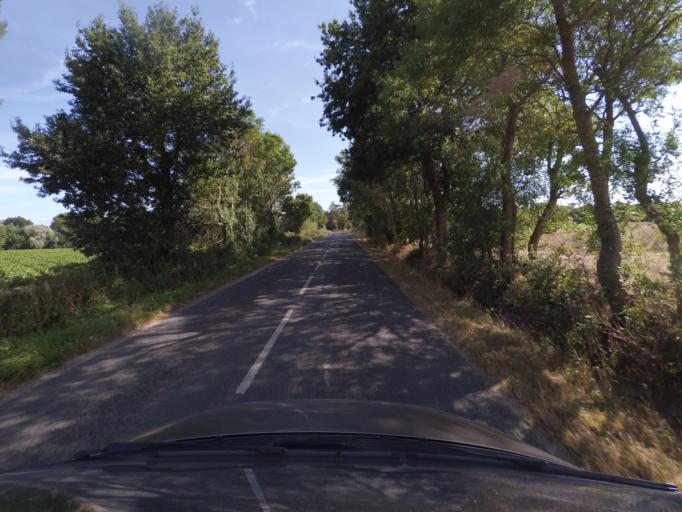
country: FR
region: Pays de la Loire
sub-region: Departement de la Loire-Atlantique
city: Les Sorinieres
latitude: 47.1213
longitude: -1.5259
